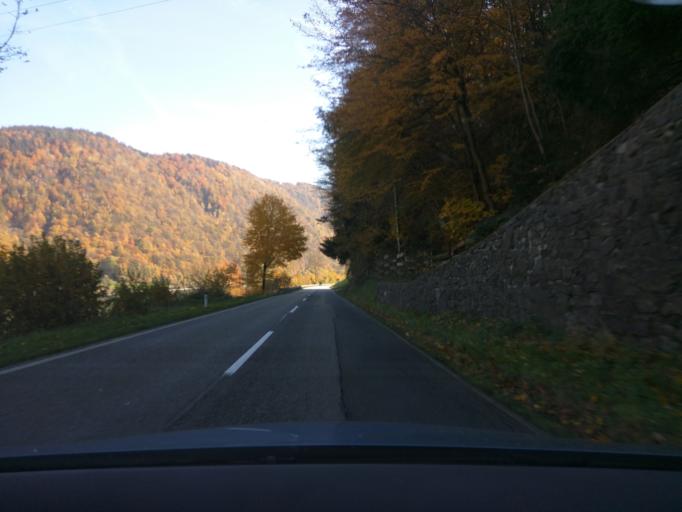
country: DE
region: Bavaria
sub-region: Lower Bavaria
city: Untergriesbach
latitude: 48.5137
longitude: 13.7186
